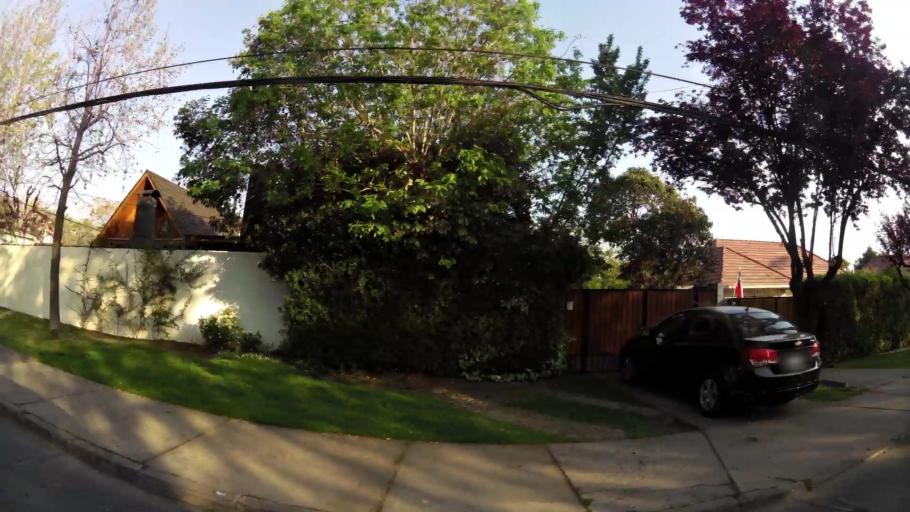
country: CL
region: Santiago Metropolitan
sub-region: Provincia de Santiago
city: Villa Presidente Frei, Nunoa, Santiago, Chile
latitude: -33.3928
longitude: -70.5493
